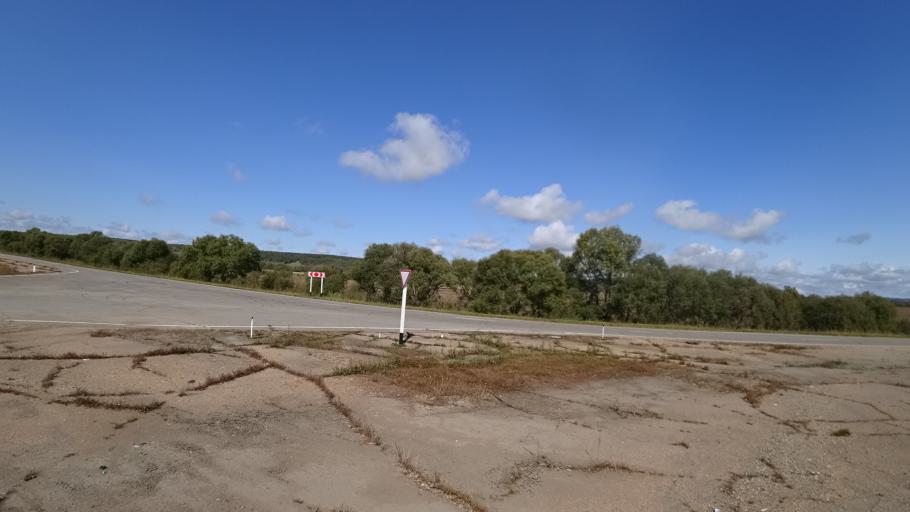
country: RU
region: Amur
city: Arkhara
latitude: 49.4138
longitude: 130.1705
